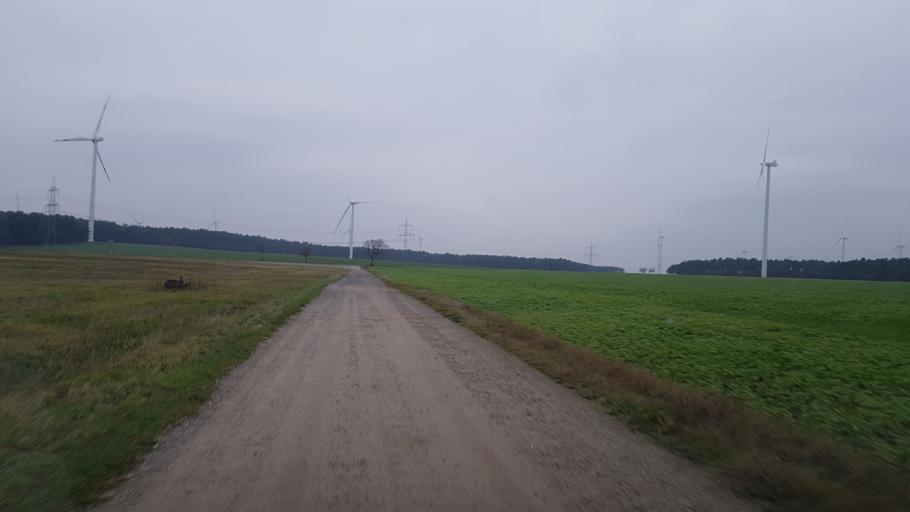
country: DE
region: Brandenburg
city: Schilda
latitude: 51.6531
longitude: 13.3777
